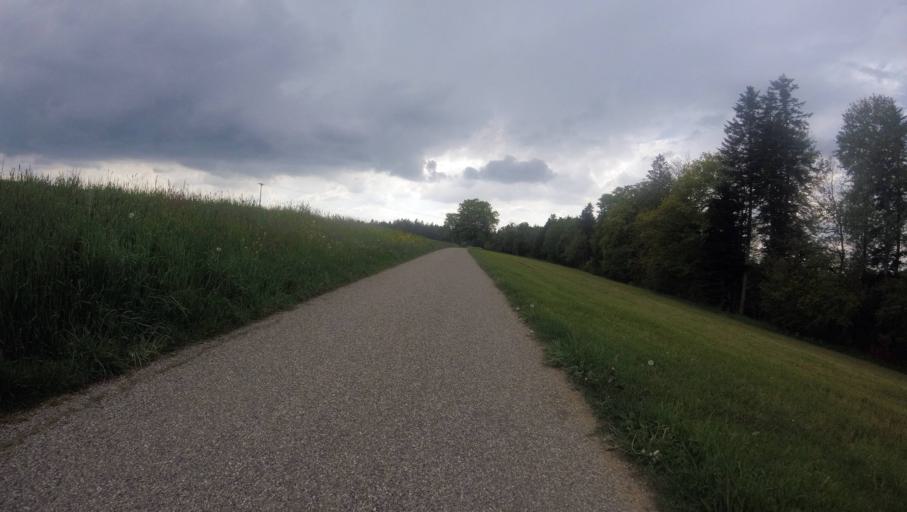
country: DE
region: Baden-Wuerttemberg
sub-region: Regierungsbezirk Stuttgart
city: Kaisersbach
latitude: 48.9323
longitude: 9.6331
